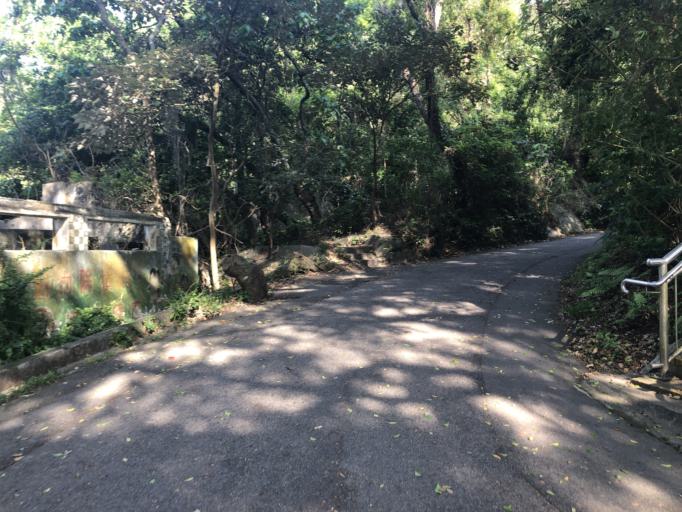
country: HK
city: Hong Kong
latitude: 22.2778
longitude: 114.1198
